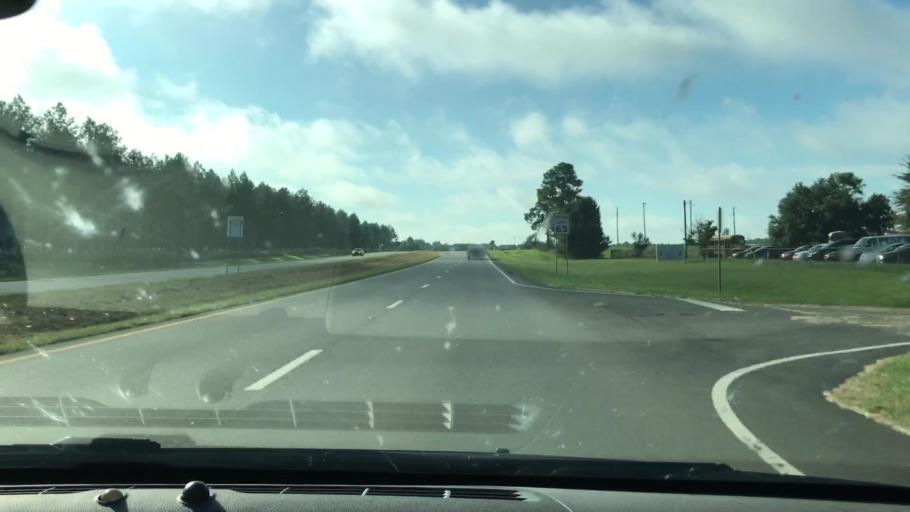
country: US
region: Georgia
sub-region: Terrell County
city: Dawson
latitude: 31.7496
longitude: -84.4208
